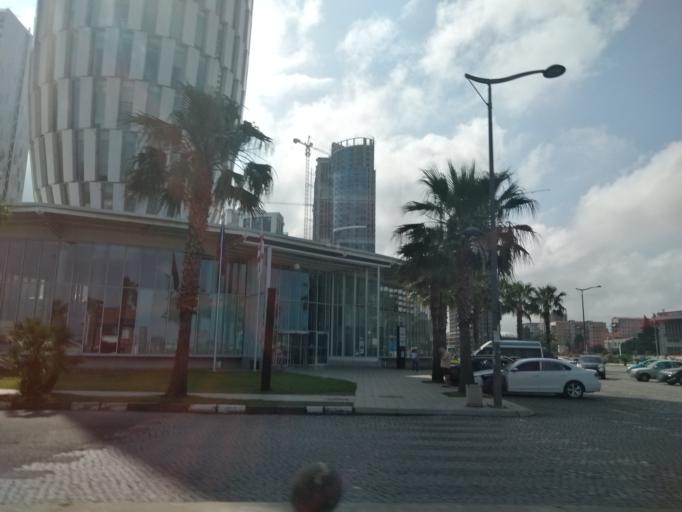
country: GE
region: Ajaria
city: Batumi
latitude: 41.6413
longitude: 41.6146
